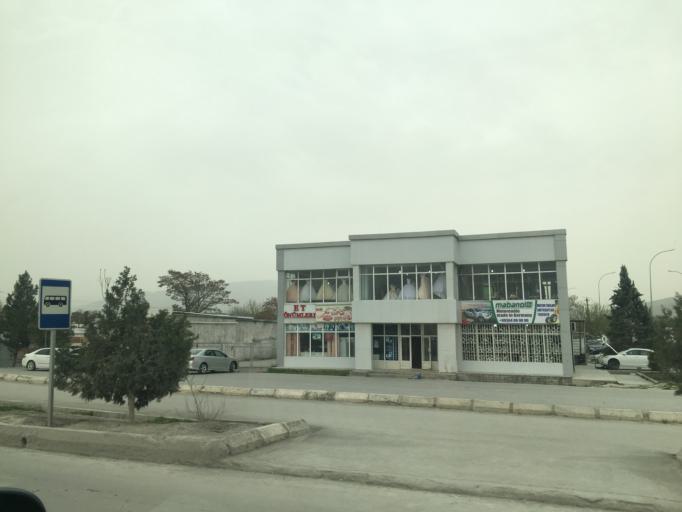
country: TM
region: Ahal
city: Abadan
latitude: 38.1609
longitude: 57.9613
